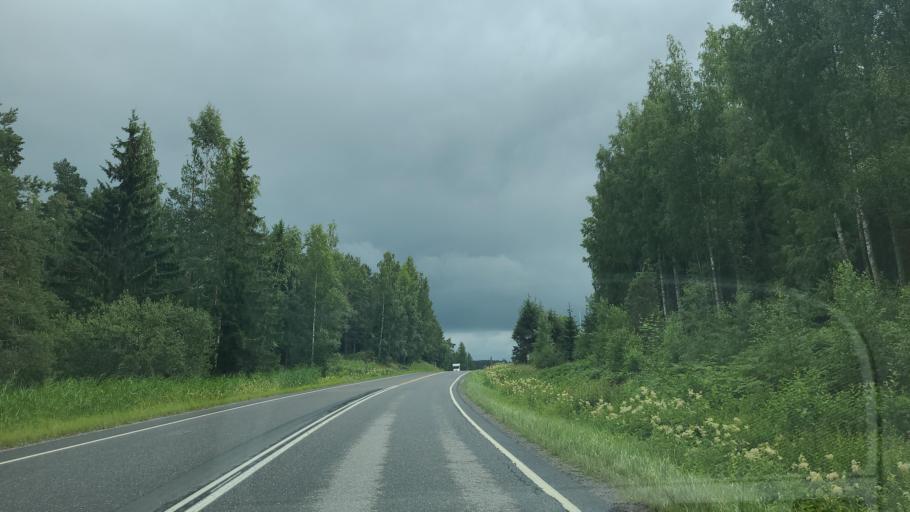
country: FI
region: Varsinais-Suomi
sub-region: Turku
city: Sauvo
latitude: 60.3383
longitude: 22.7015
